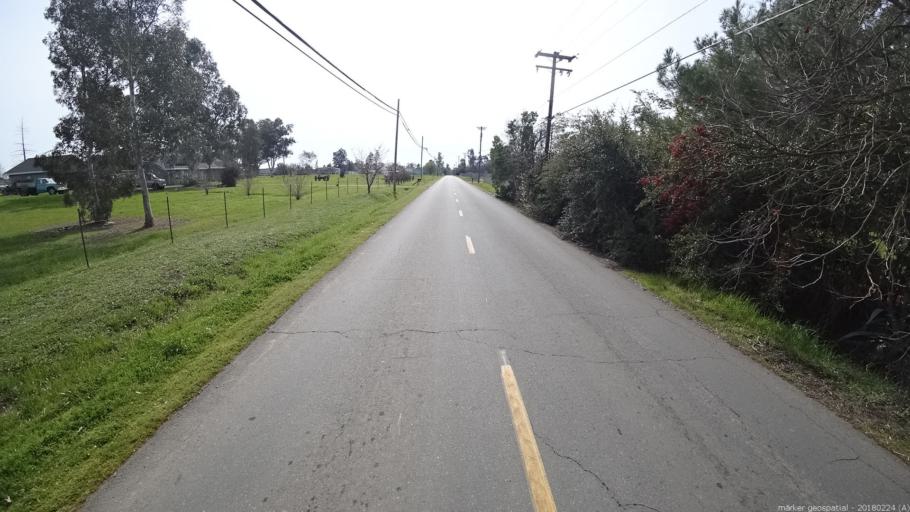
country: US
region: California
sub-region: Sacramento County
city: Elverta
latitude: 38.7098
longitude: -121.4666
